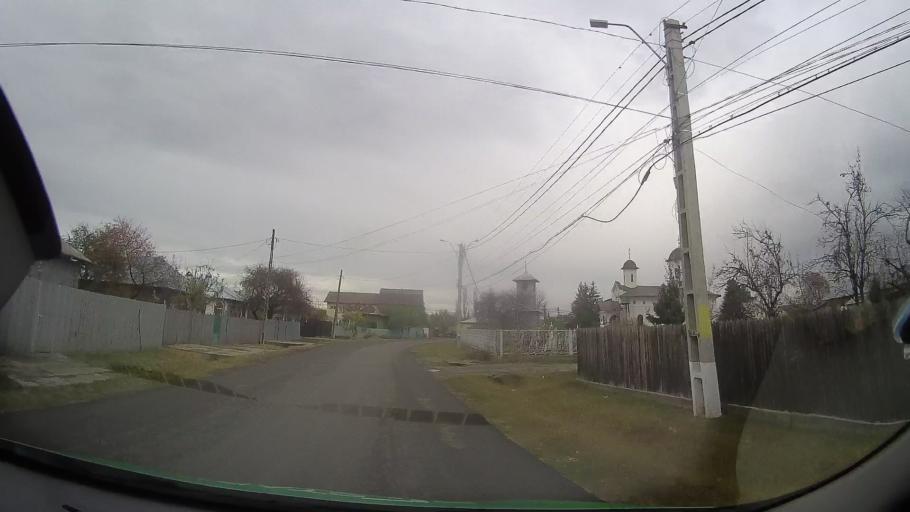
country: RO
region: Prahova
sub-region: Comuna Colceag
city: Inotesti
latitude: 44.9598
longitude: 26.3583
